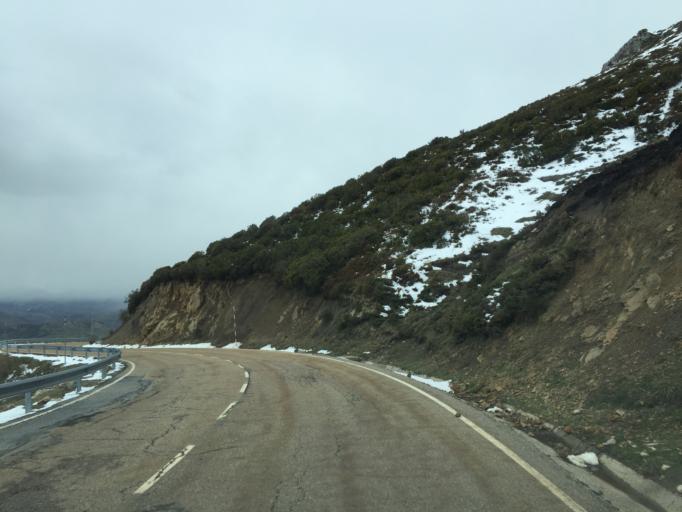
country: ES
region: Castille and Leon
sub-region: Provincia de Leon
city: San Emiliano
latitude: 43.0558
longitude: -6.0068
